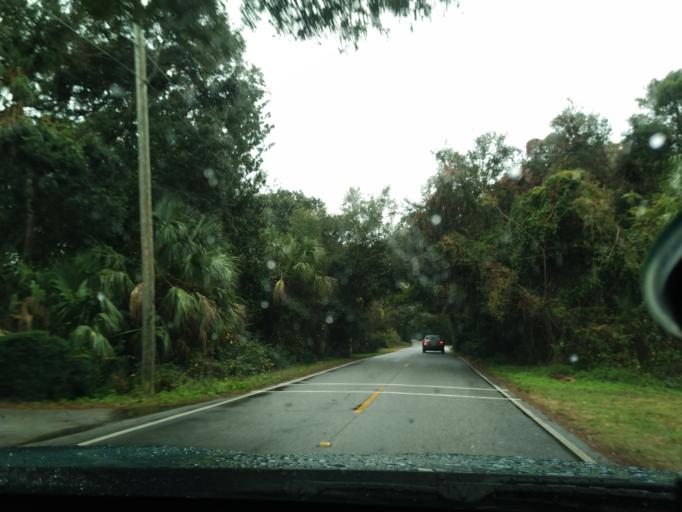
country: US
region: South Carolina
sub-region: Charleston County
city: Folly Beach
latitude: 32.6654
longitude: -79.9175
